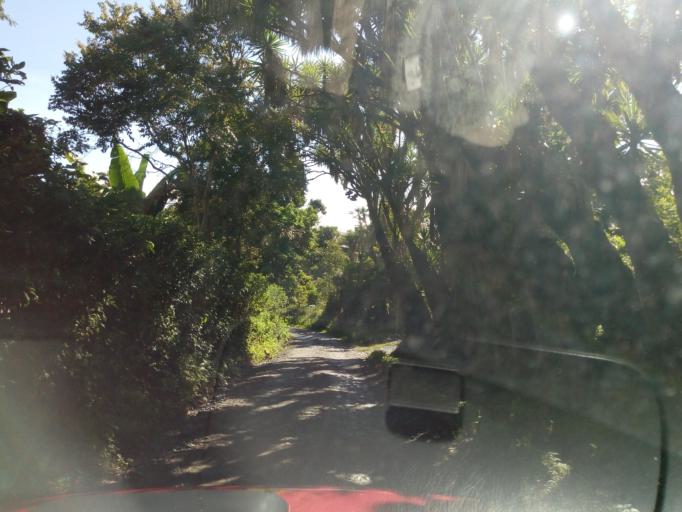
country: CO
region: Boyaca
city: Moniquira
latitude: 5.8934
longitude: -73.5337
